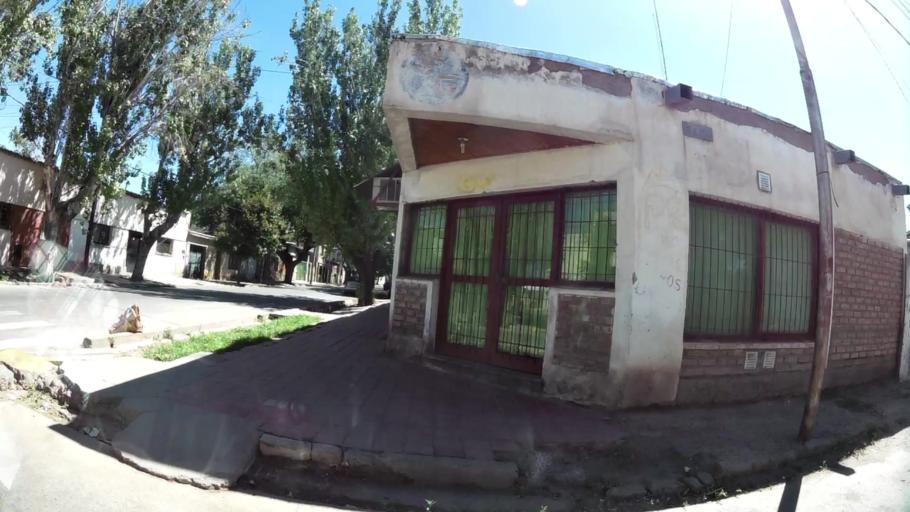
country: AR
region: Mendoza
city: Las Heras
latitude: -32.8537
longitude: -68.8351
